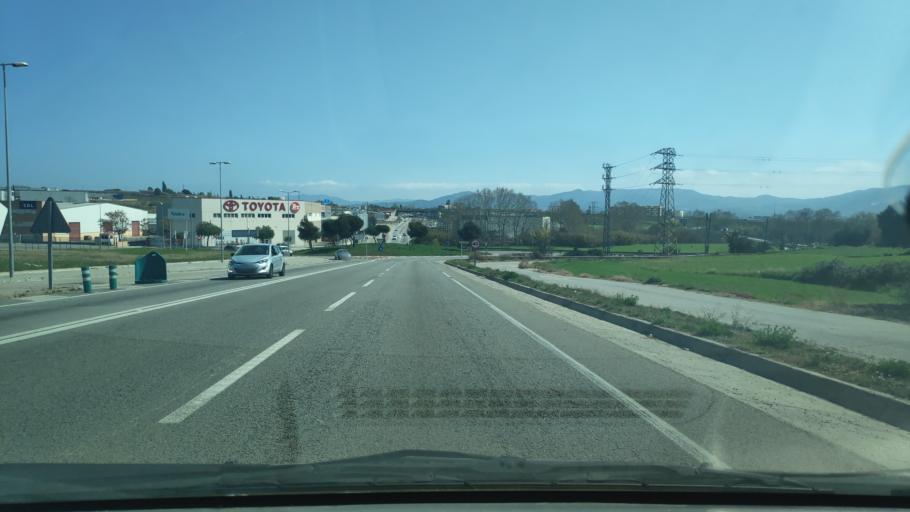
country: ES
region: Catalonia
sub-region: Provincia de Barcelona
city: Polinya
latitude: 41.5338
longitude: 2.1626
